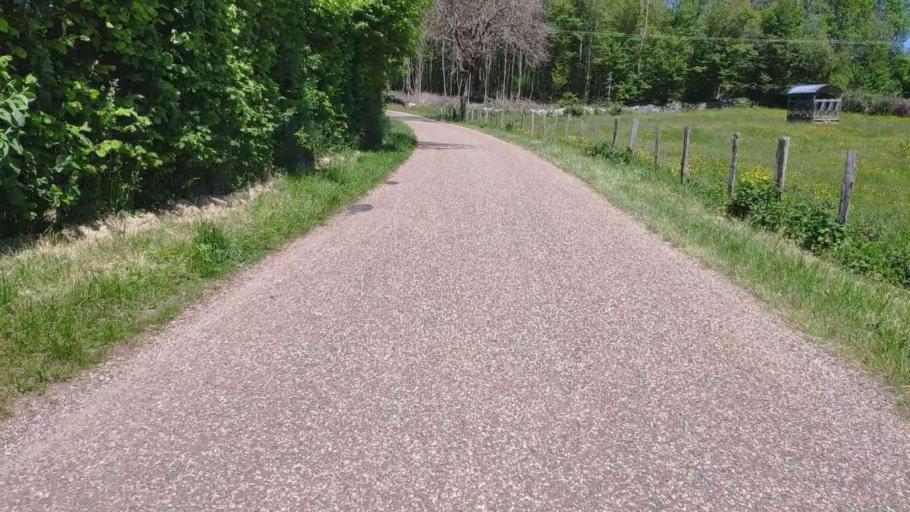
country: FR
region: Franche-Comte
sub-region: Departement du Jura
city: Poligny
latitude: 46.7405
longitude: 5.6743
